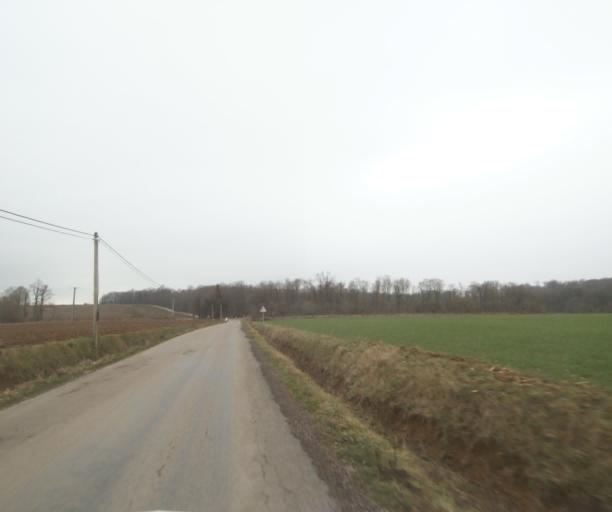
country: FR
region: Champagne-Ardenne
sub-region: Departement de la Haute-Marne
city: Wassy
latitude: 48.5388
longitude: 4.9822
